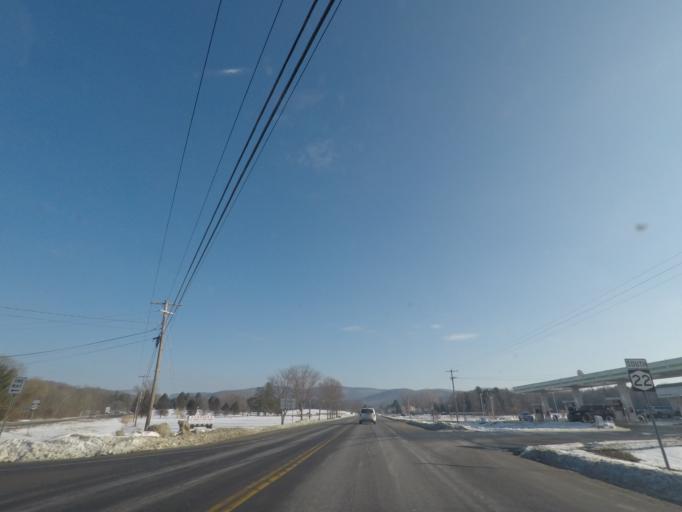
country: US
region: Massachusetts
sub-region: Berkshire County
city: Lanesborough
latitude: 42.5475
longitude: -73.3684
